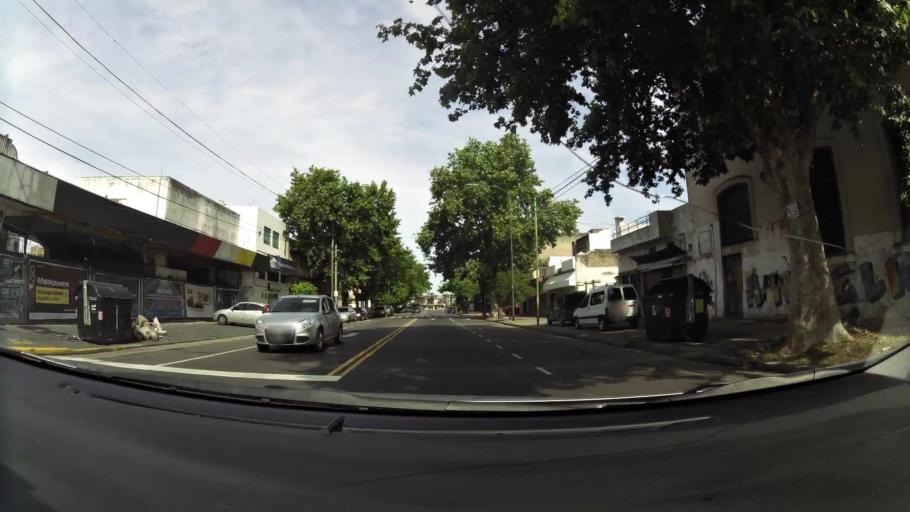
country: AR
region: Buenos Aires
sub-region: Partido de Avellaneda
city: Avellaneda
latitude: -34.6476
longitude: -58.4184
